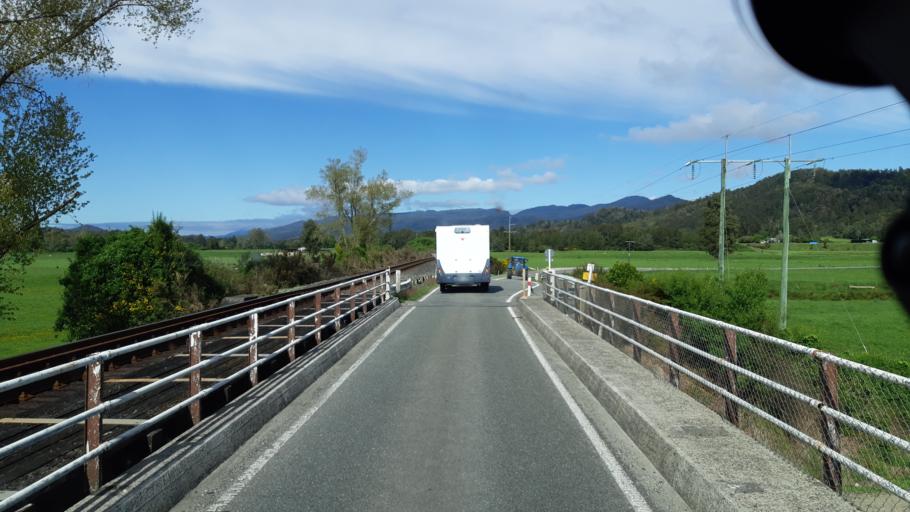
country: NZ
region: West Coast
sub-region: Buller District
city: Westport
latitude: -41.8603
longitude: 171.9447
